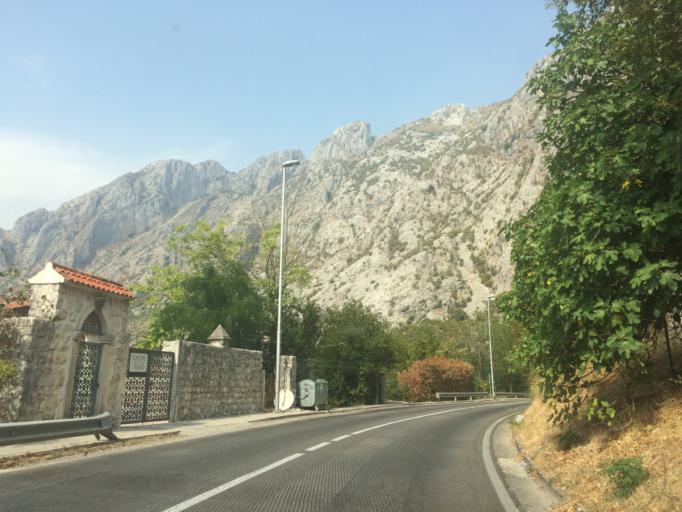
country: ME
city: Dobrota
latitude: 42.4840
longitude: 18.7656
